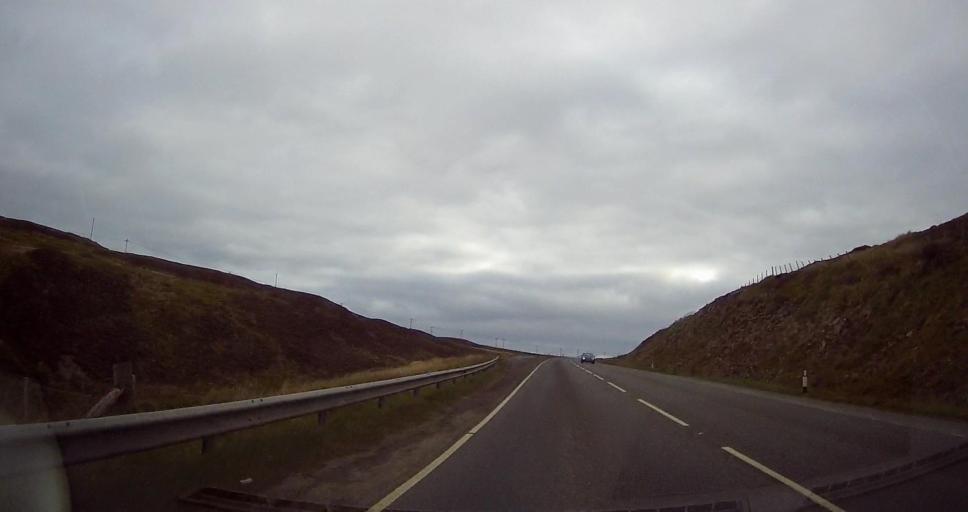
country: GB
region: Scotland
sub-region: Shetland Islands
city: Lerwick
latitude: 60.1658
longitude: -1.2085
